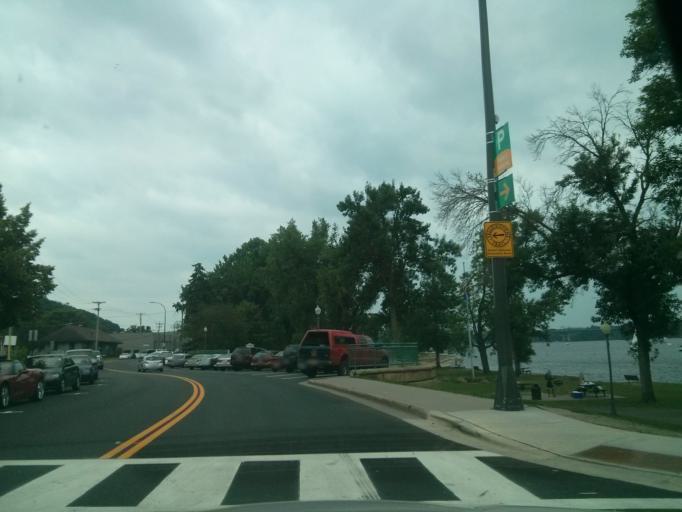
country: US
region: Wisconsin
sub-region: Saint Croix County
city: Hudson
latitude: 44.9748
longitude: -92.7585
